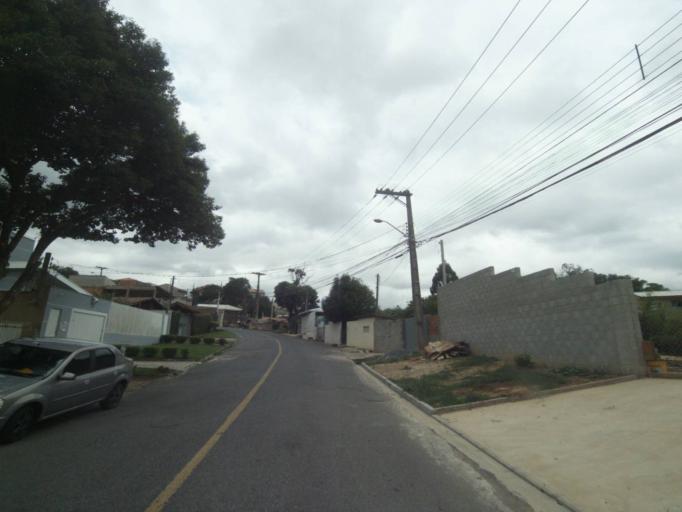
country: BR
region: Parana
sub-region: Curitiba
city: Curitiba
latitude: -25.3872
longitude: -49.2889
